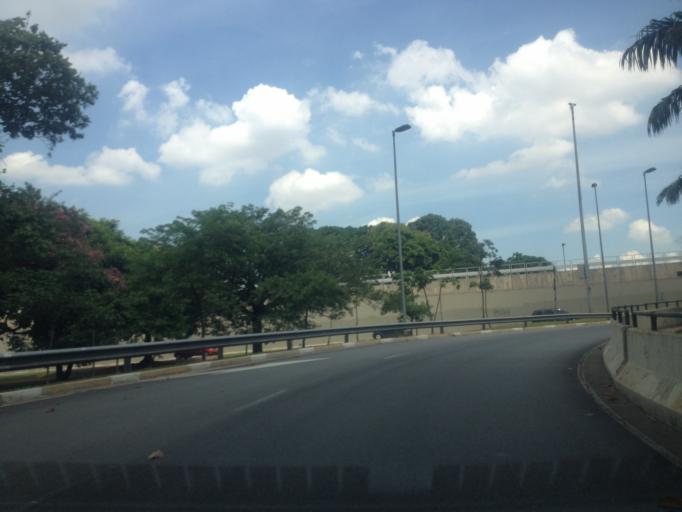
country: BR
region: Sao Paulo
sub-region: Sao Paulo
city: Sao Paulo
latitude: -23.5209
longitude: -46.6245
